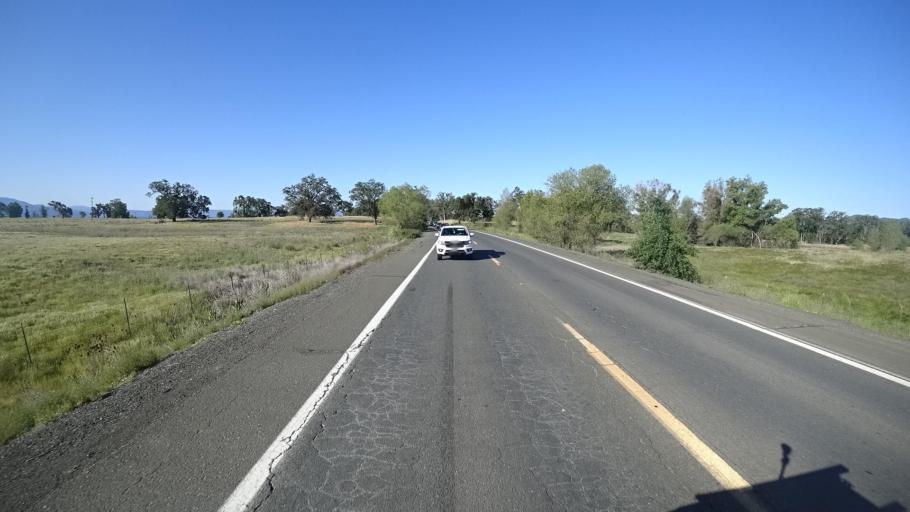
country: US
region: California
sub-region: Lake County
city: Nice
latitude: 39.1261
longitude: -122.8743
